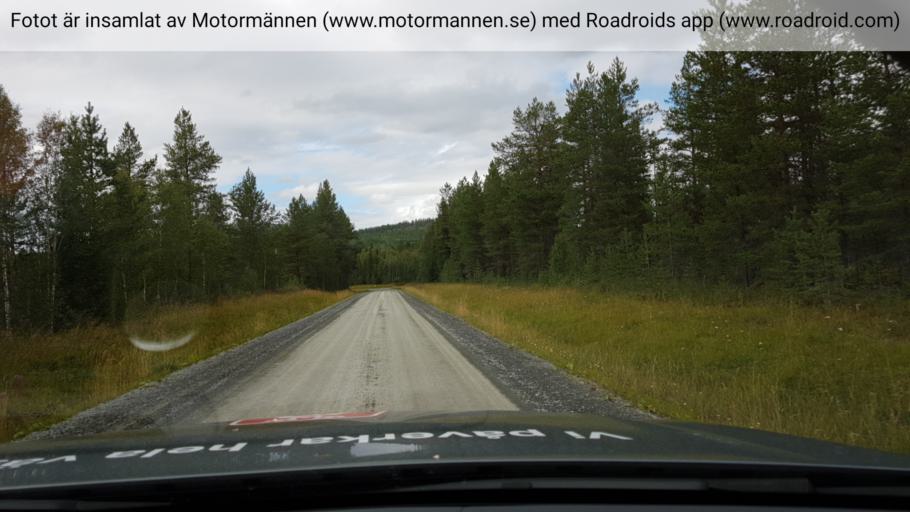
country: SE
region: Jaemtland
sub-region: Krokoms Kommun
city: Valla
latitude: 63.7053
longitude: 13.5939
